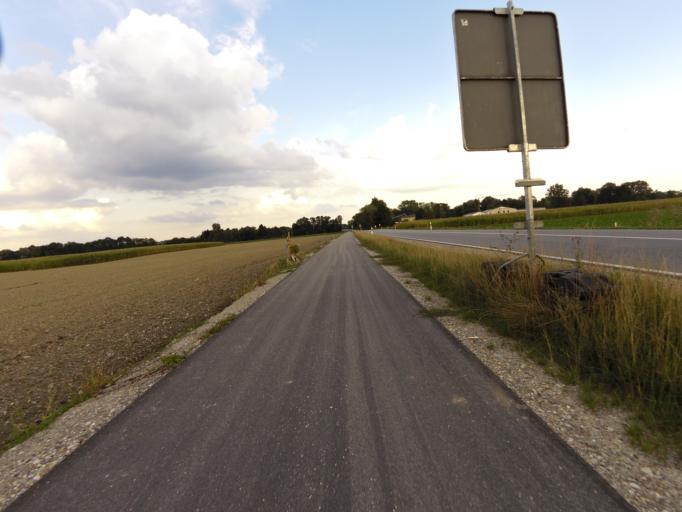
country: DE
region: Bavaria
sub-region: Upper Bavaria
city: Moosburg
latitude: 48.4641
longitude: 11.9653
